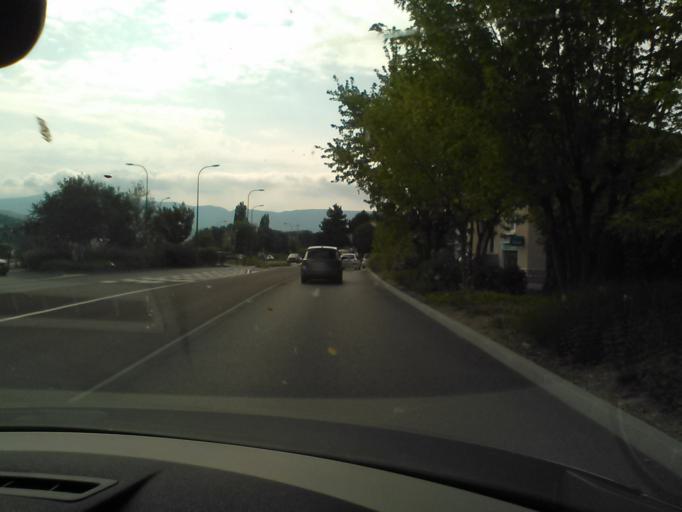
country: FR
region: Rhone-Alpes
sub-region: Departement de la Savoie
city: Saint-Alban-Leysse
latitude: 45.5734
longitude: 5.9478
